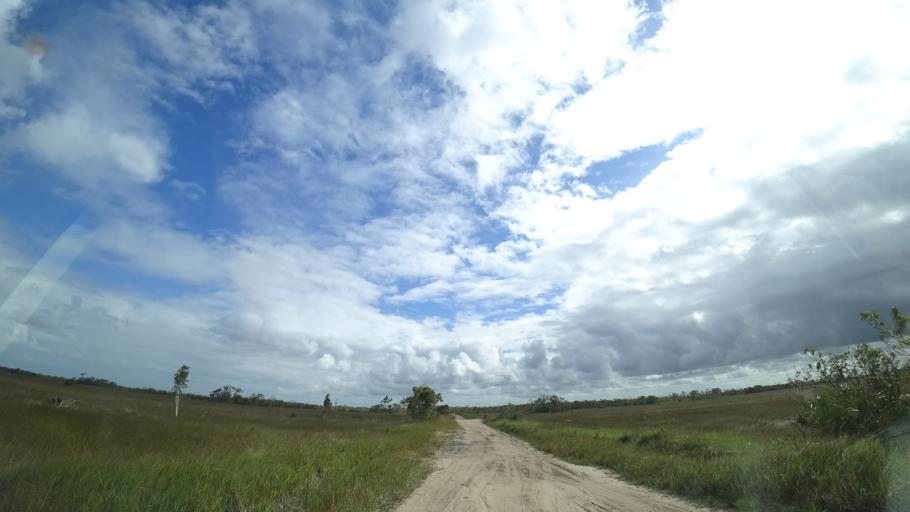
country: MZ
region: Sofala
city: Beira
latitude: -19.5786
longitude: 35.1853
